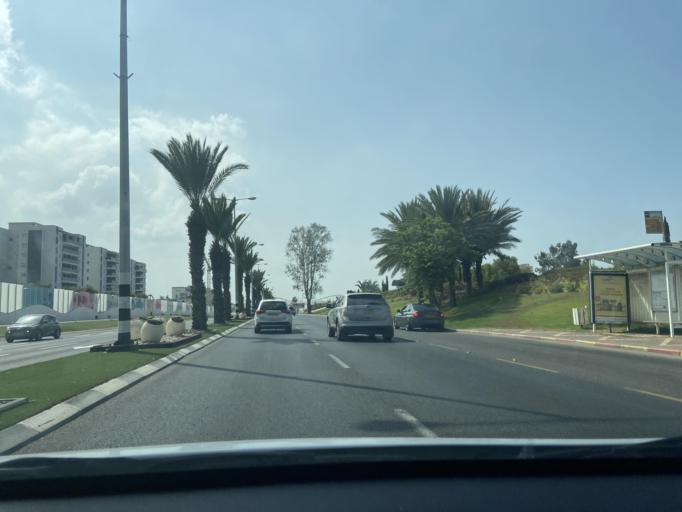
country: IL
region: Northern District
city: Nahariya
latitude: 33.0017
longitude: 35.0986
